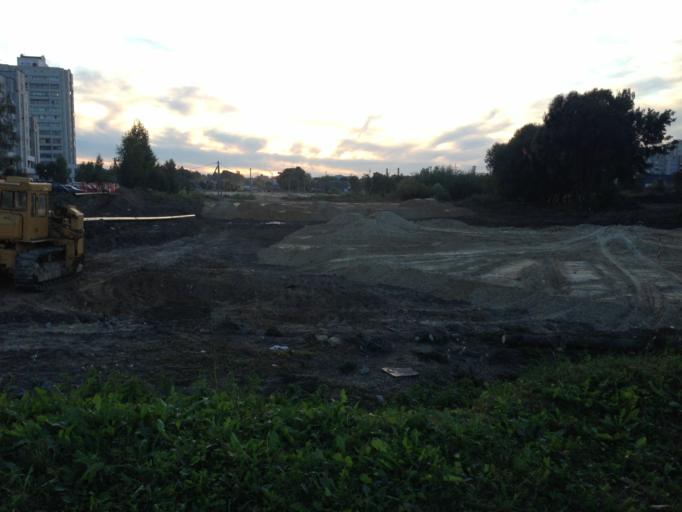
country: BY
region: Grodnenskaya
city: Hrodna
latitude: 53.7068
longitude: 23.8493
